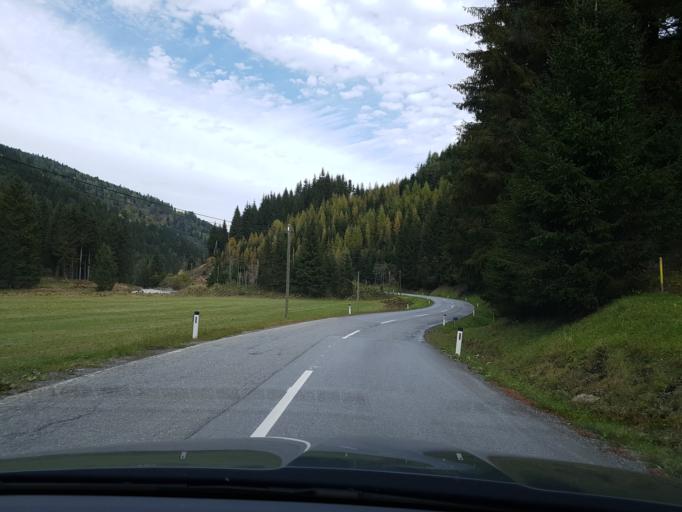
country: AT
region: Salzburg
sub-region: Politischer Bezirk Tamsweg
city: Ramingstein
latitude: 47.0171
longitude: 13.8990
